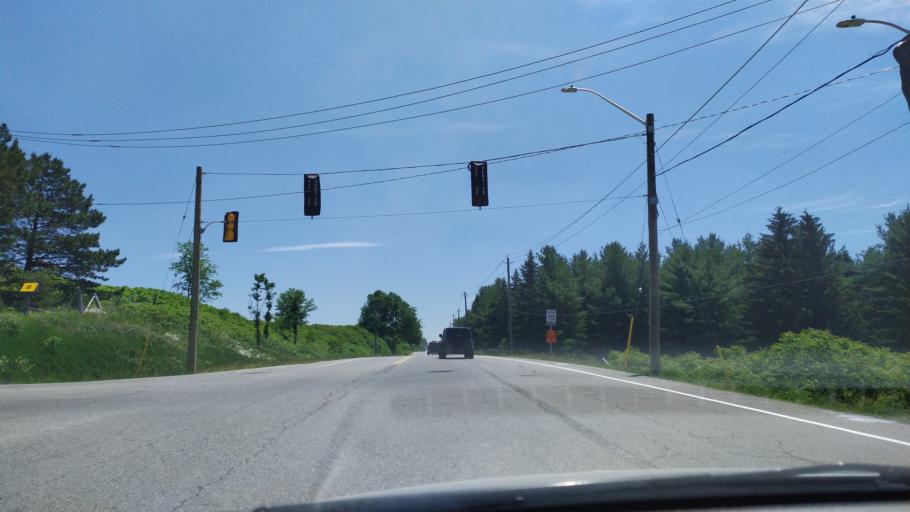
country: CA
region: Ontario
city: Kitchener
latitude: 43.3969
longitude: -80.5349
